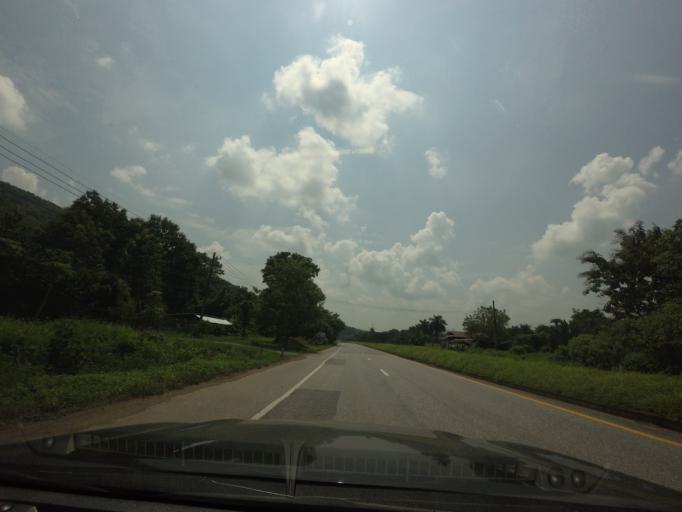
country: TH
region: Uttaradit
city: Lap Lae
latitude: 17.7933
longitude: 100.1167
